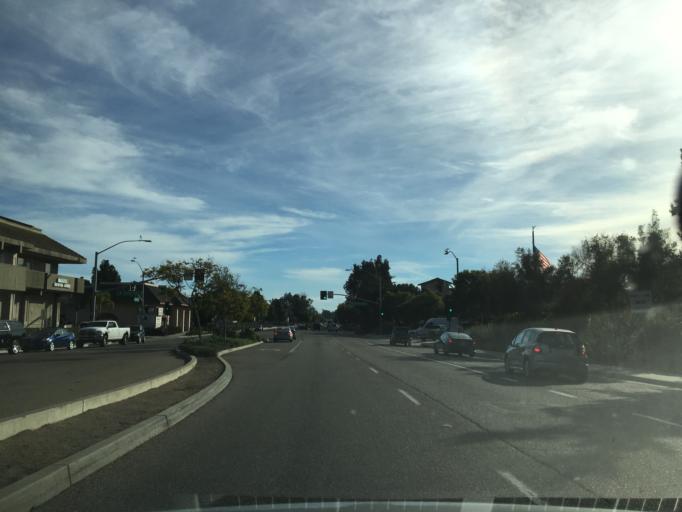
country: US
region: California
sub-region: Santa Barbara County
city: Isla Vista
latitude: 34.4295
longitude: -119.8698
